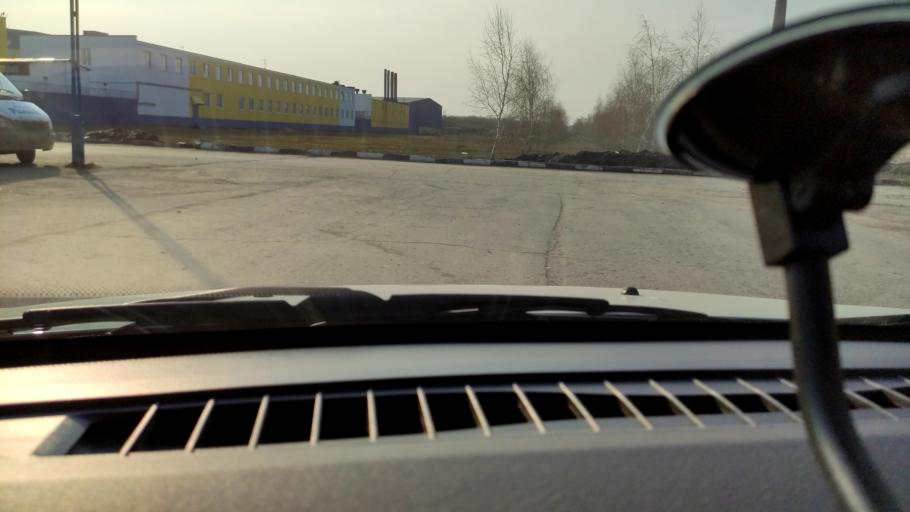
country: RU
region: Samara
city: Samara
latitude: 53.1837
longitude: 50.2623
